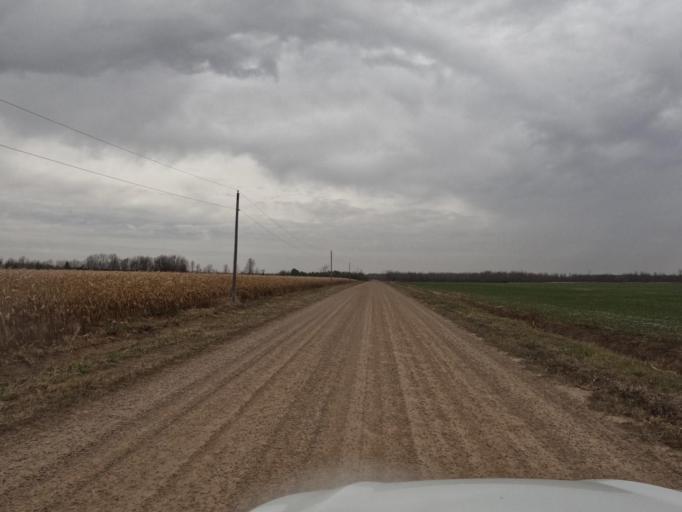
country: CA
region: Ontario
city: Shelburne
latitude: 43.8877
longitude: -80.3826
